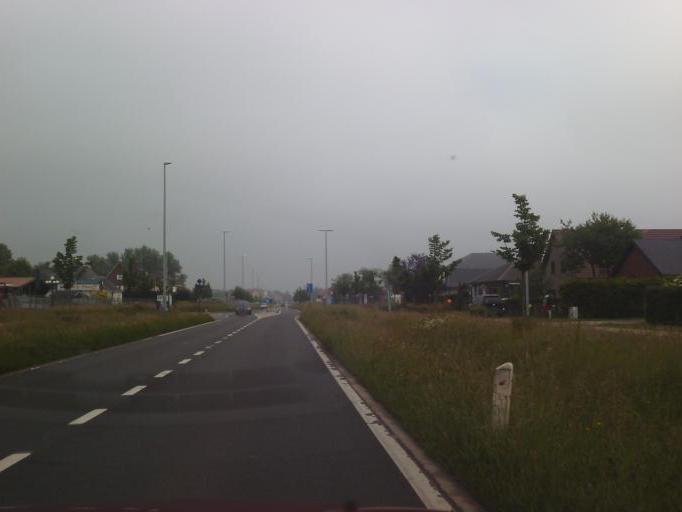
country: BE
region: Flanders
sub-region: Provincie Oost-Vlaanderen
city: Aalst
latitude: 50.9734
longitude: 4.0428
